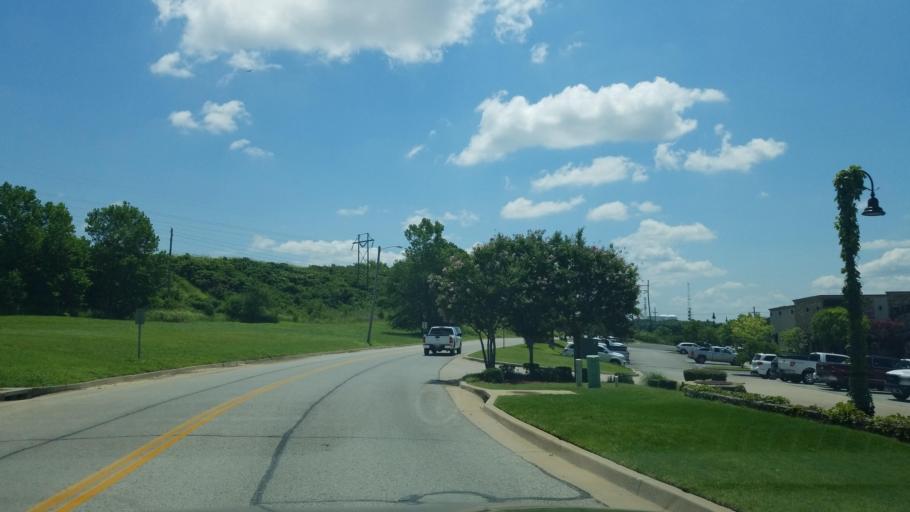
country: US
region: Oklahoma
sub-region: Tulsa County
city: Broken Arrow
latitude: 36.0703
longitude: -95.7898
